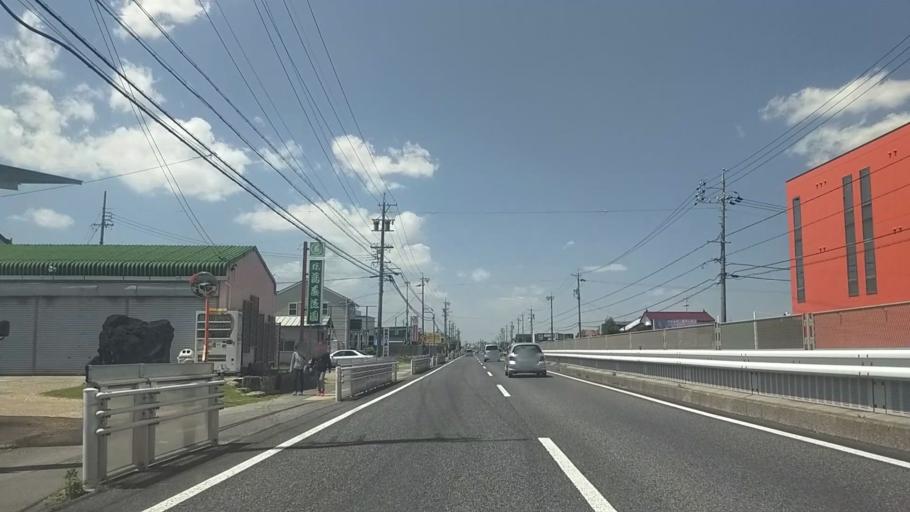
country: JP
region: Aichi
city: Okazaki
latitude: 34.9196
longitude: 137.2074
